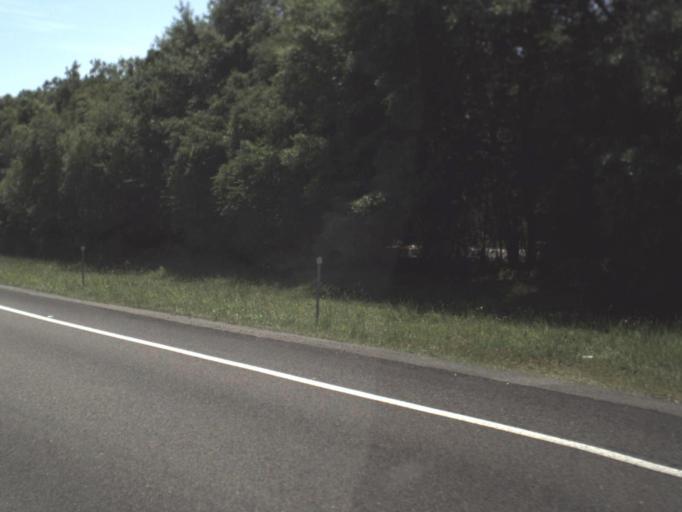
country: US
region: Florida
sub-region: Clay County
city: Bellair-Meadowbrook Terrace
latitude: 30.2518
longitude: -81.7631
